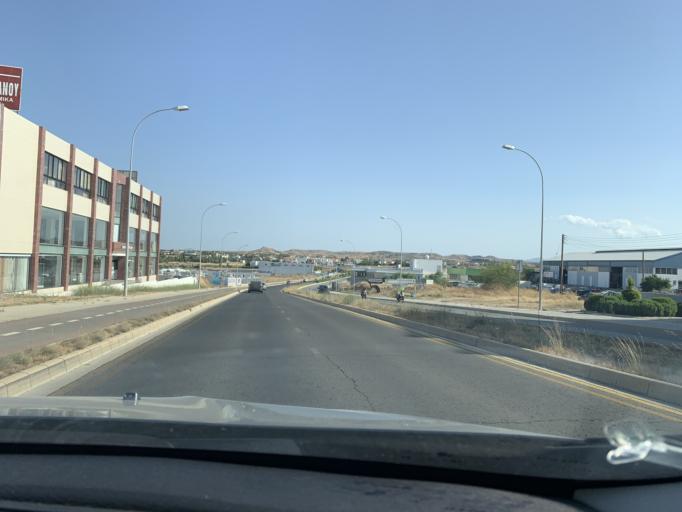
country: CY
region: Lefkosia
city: Nicosia
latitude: 35.1208
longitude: 33.3565
